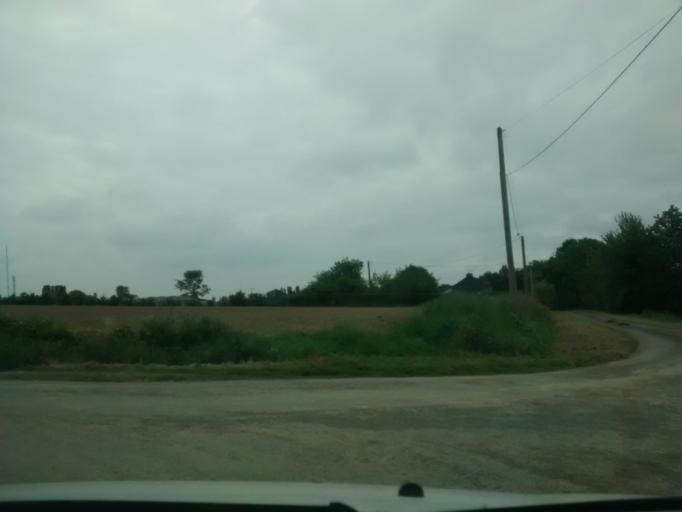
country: FR
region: Brittany
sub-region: Departement d'Ille-et-Vilaine
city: Chantepie
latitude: 48.0907
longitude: -1.5907
